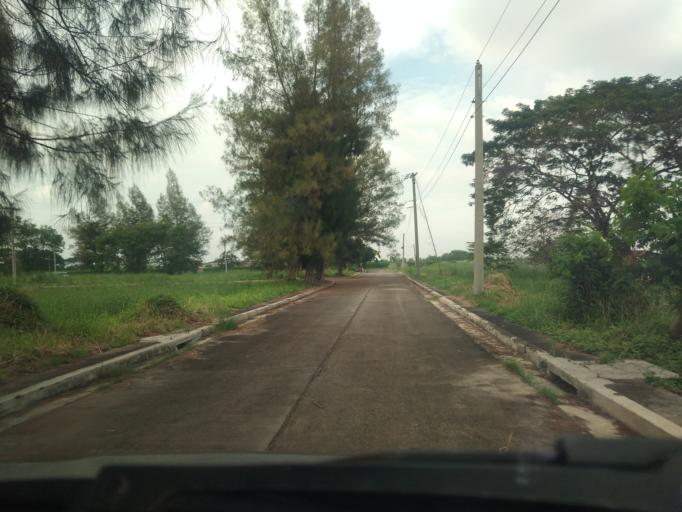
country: PH
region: Central Luzon
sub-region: Province of Pampanga
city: Santo Domingo
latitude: 15.0044
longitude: 120.7264
